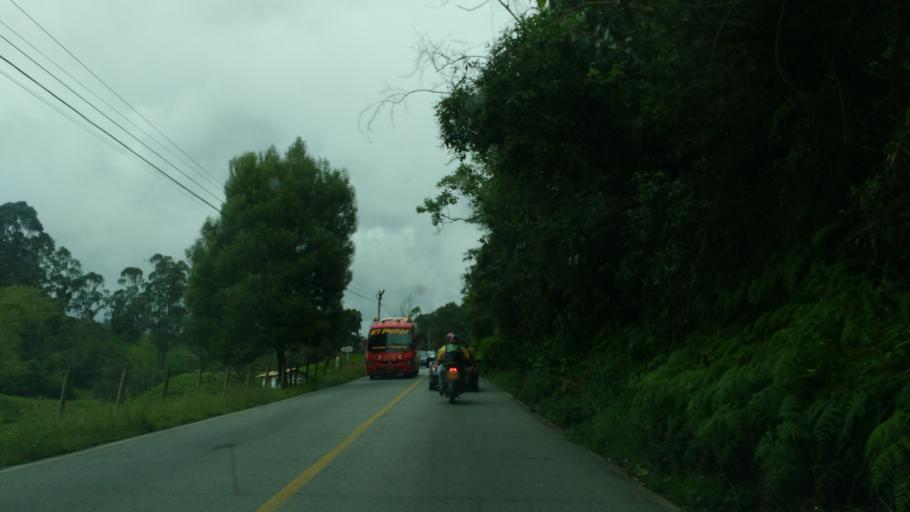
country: CO
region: Antioquia
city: Marinilla
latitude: 6.1977
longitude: -75.2850
